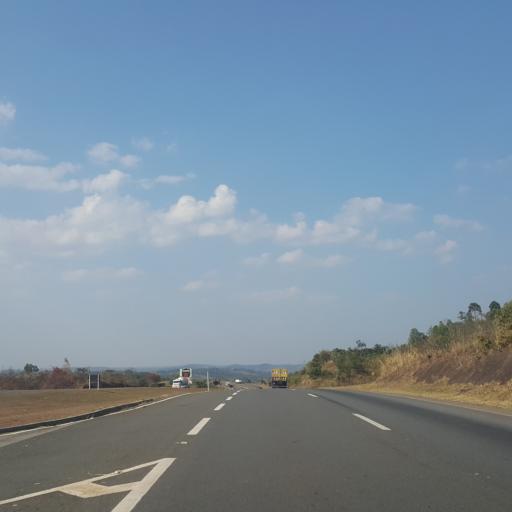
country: BR
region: Goias
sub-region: Abadiania
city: Abadiania
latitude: -16.1859
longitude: -48.6605
